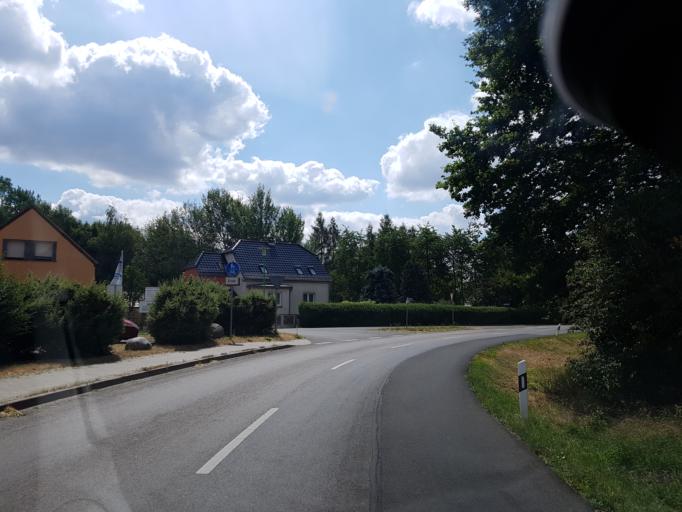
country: DE
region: Brandenburg
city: Drebkau
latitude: 51.6905
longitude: 14.2699
